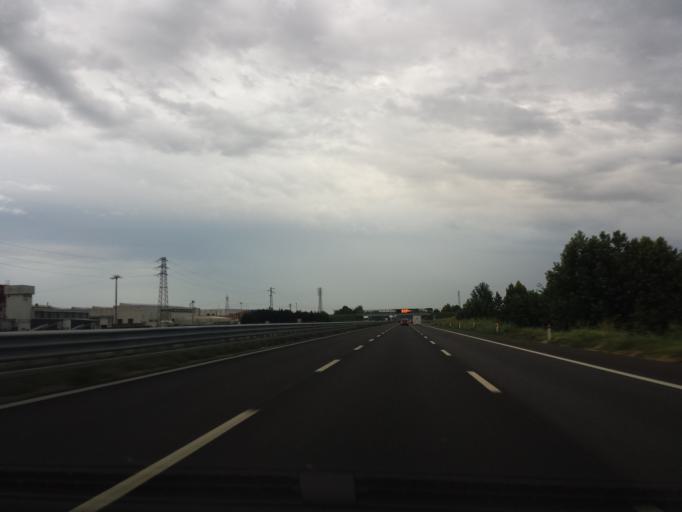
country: IT
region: Veneto
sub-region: Provincia di Vicenza
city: Torri di Quartesolo
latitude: 45.4976
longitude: 11.6471
